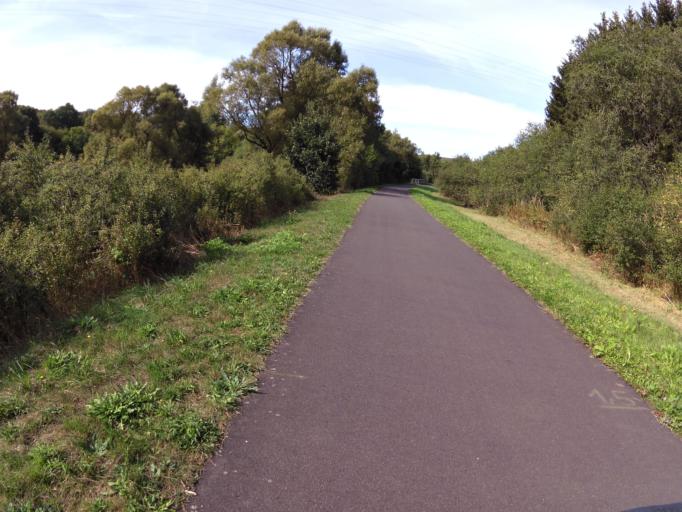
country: DE
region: Rheinland-Pfalz
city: Pronsfeld
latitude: 50.1637
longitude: 6.3186
